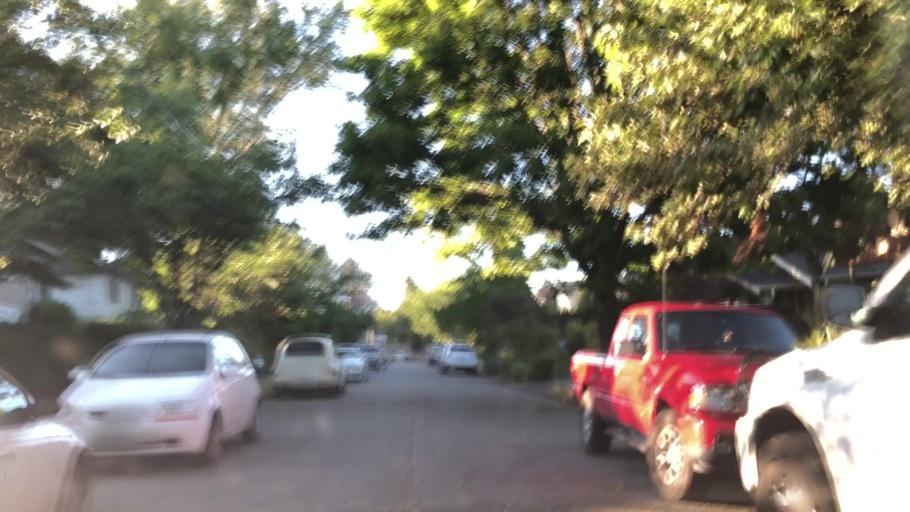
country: US
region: Washington
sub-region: King County
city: Seattle
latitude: 47.6566
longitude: -122.3279
